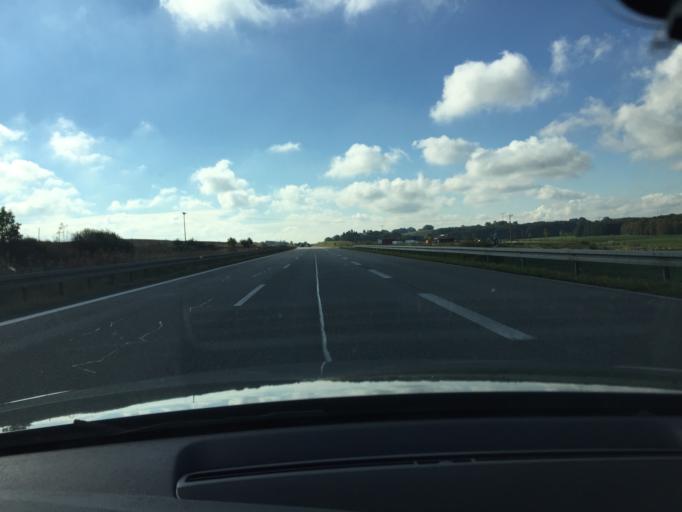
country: DE
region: Mecklenburg-Vorpommern
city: Lalendorf
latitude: 53.7173
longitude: 12.3569
